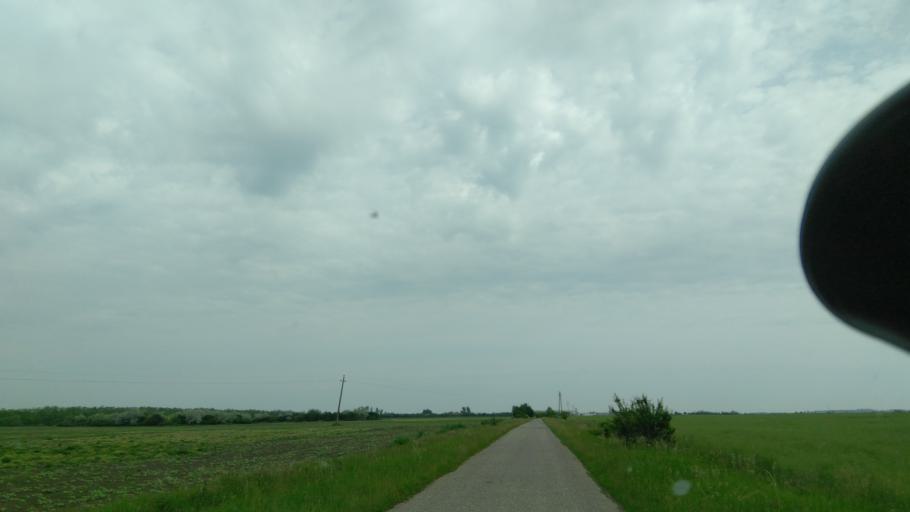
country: HU
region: Bekes
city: Szeghalom
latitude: 47.0392
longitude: 21.1544
